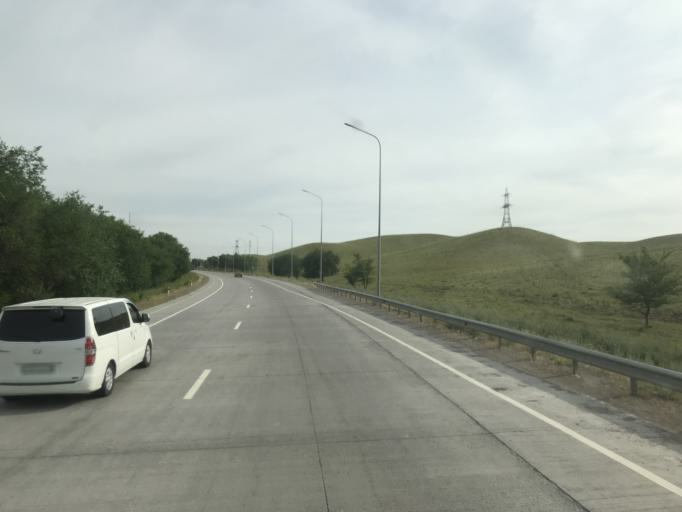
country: KZ
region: Ongtustik Qazaqstan
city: Shymkent
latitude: 42.2229
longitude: 69.5328
